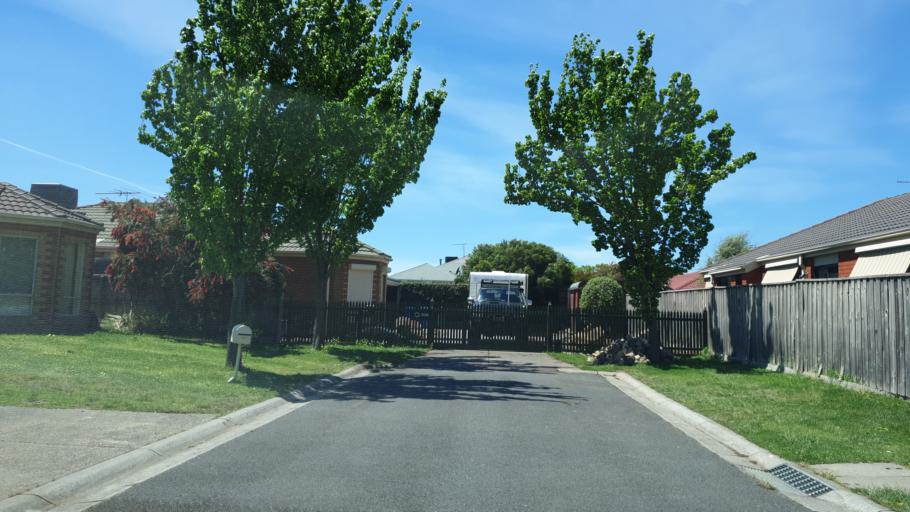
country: AU
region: Victoria
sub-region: Casey
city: Narre Warren South
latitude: -38.0607
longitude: 145.2836
